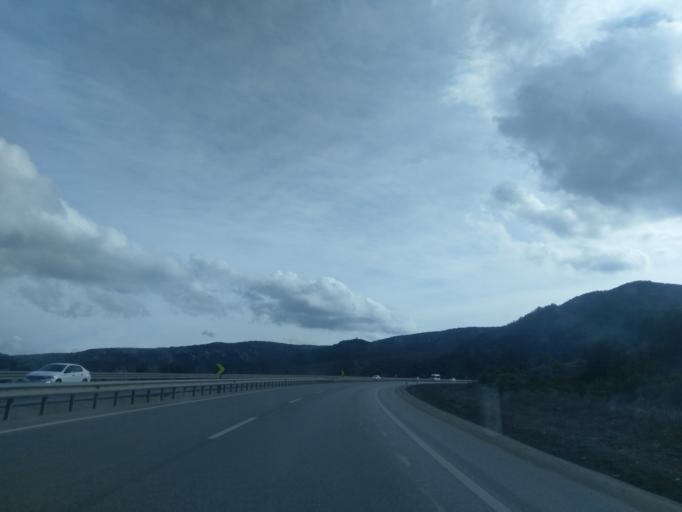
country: TR
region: Kuetahya
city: Sabuncu
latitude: 39.5620
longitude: 30.0762
